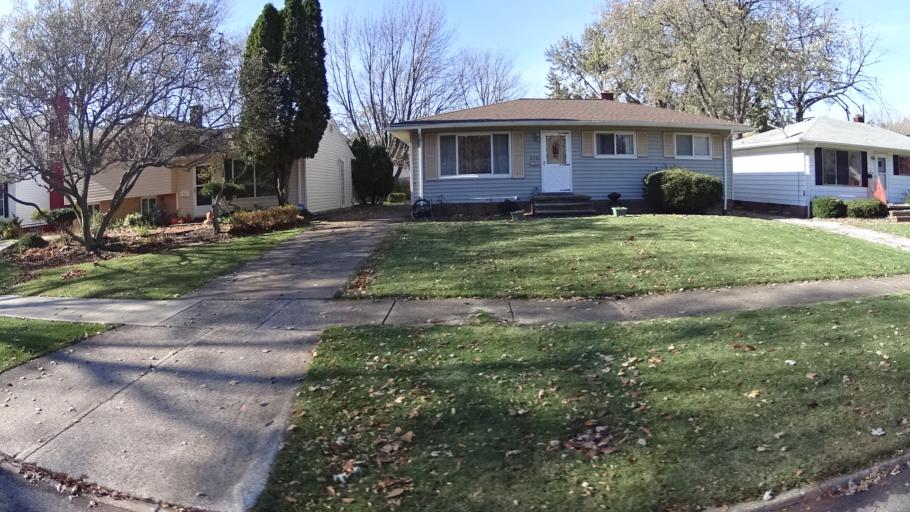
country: US
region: Ohio
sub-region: Lorain County
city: Sheffield Lake
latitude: 41.4977
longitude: -82.0678
